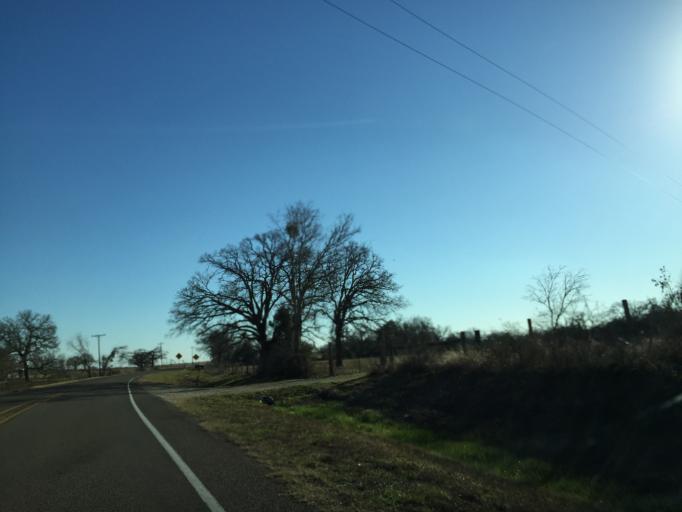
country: US
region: Texas
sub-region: Bastrop County
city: Elgin
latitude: 30.3862
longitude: -97.2437
